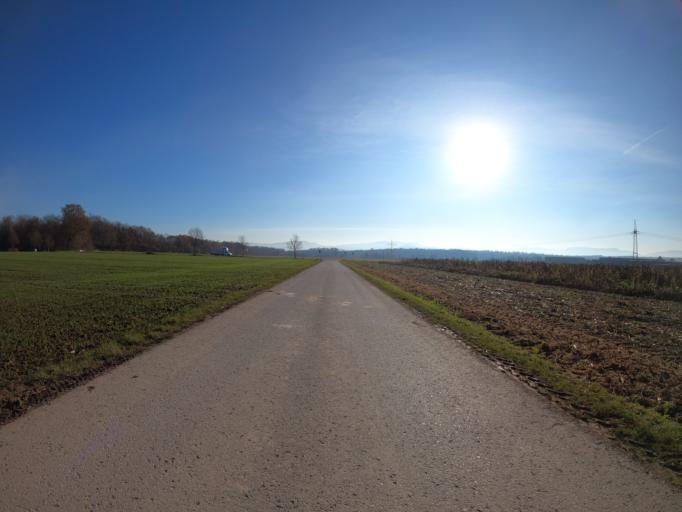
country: DE
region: Baden-Wuerttemberg
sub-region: Regierungsbezirk Stuttgart
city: Schlierbach
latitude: 48.6825
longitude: 9.5372
